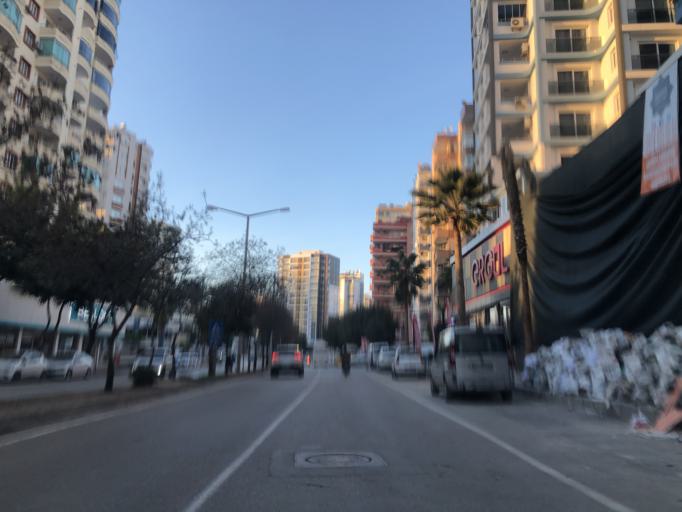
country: TR
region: Adana
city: Adana
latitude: 37.0343
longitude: 35.2992
